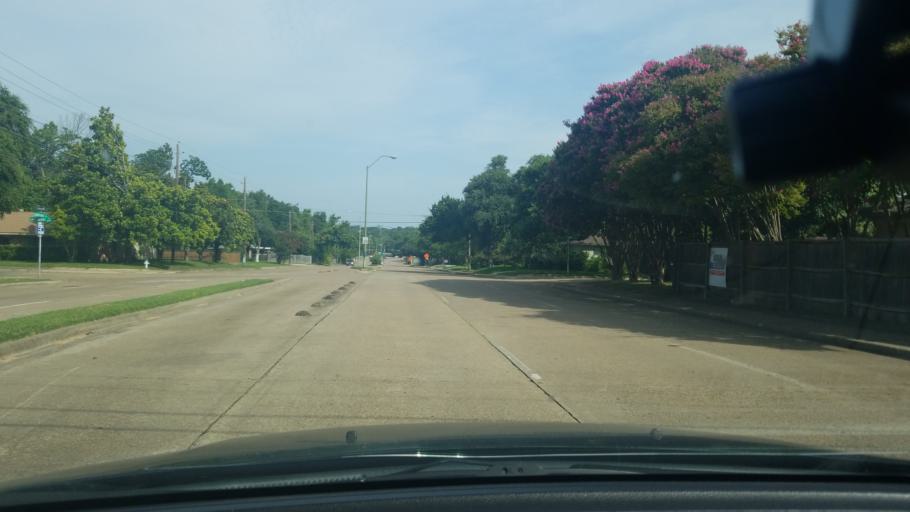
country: US
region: Texas
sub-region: Dallas County
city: Highland Park
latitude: 32.8085
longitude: -96.6972
